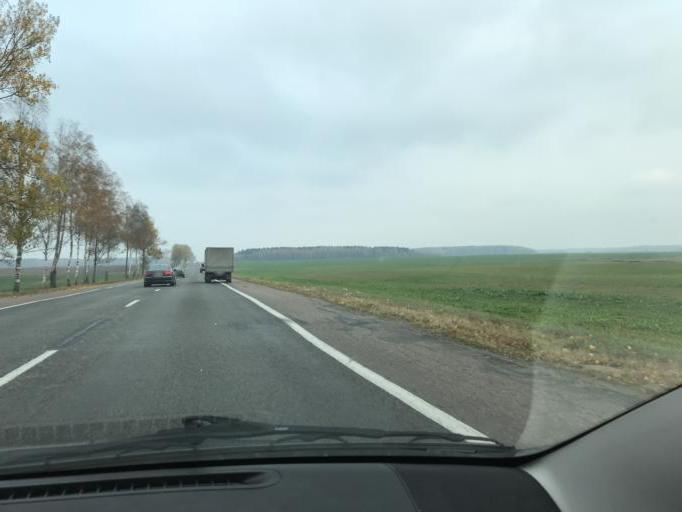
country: BY
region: Vitebsk
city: Syanno
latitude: 55.0854
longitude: 29.5996
